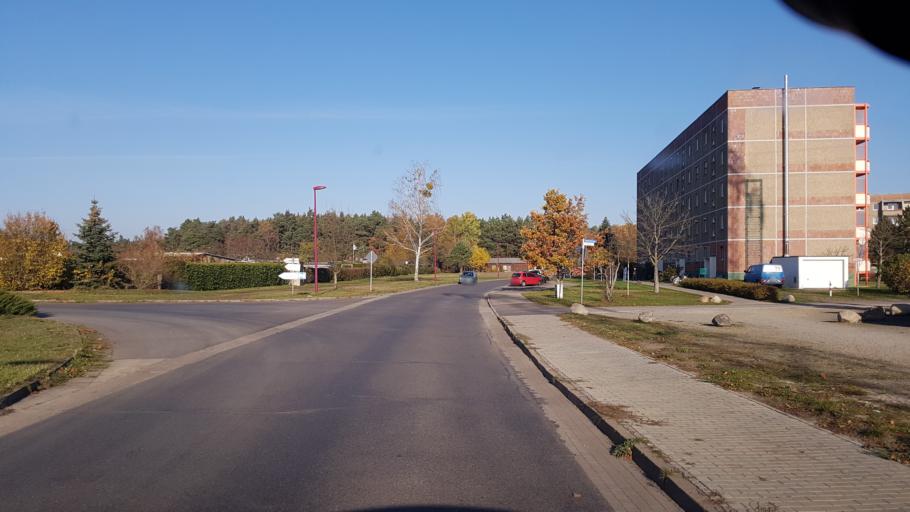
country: DE
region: Brandenburg
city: Grossraschen
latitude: 51.5915
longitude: 13.9982
